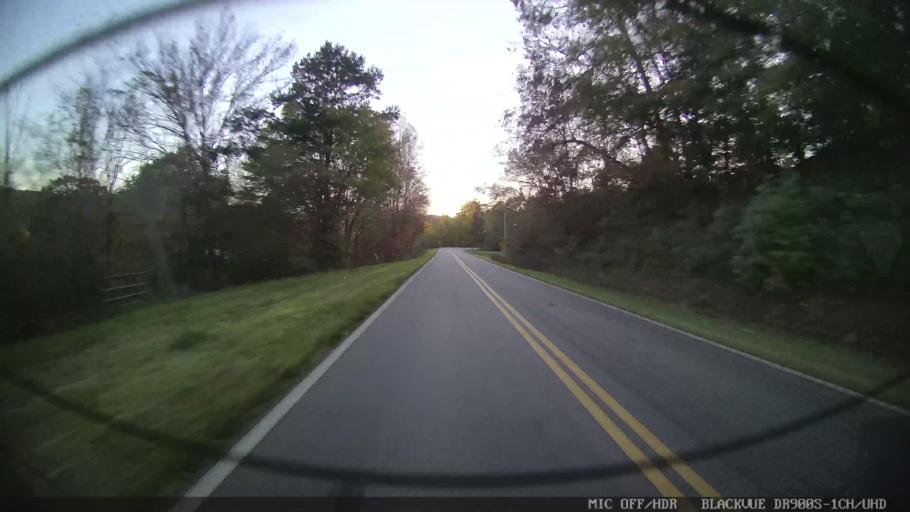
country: US
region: Georgia
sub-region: Union County
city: Blairsville
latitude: 34.8478
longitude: -83.9238
